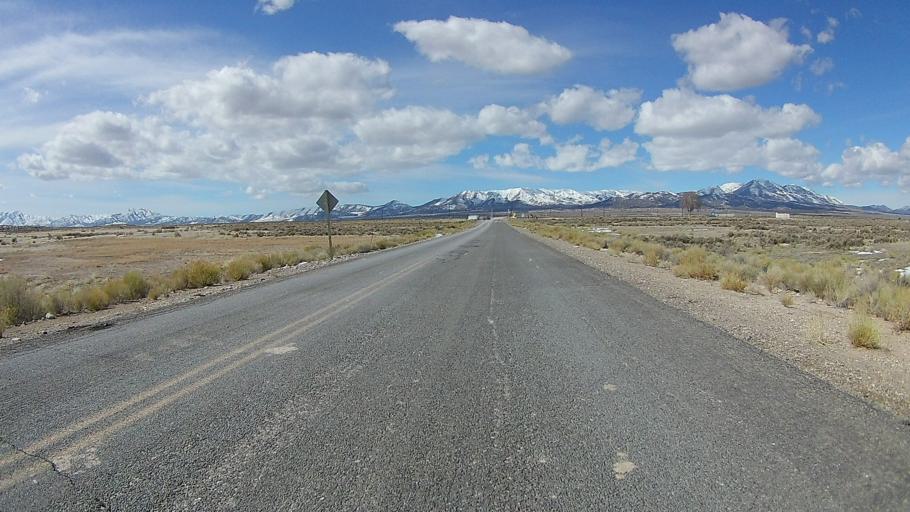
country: US
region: Utah
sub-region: Tooele County
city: Tooele
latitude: 40.1830
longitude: -112.3878
